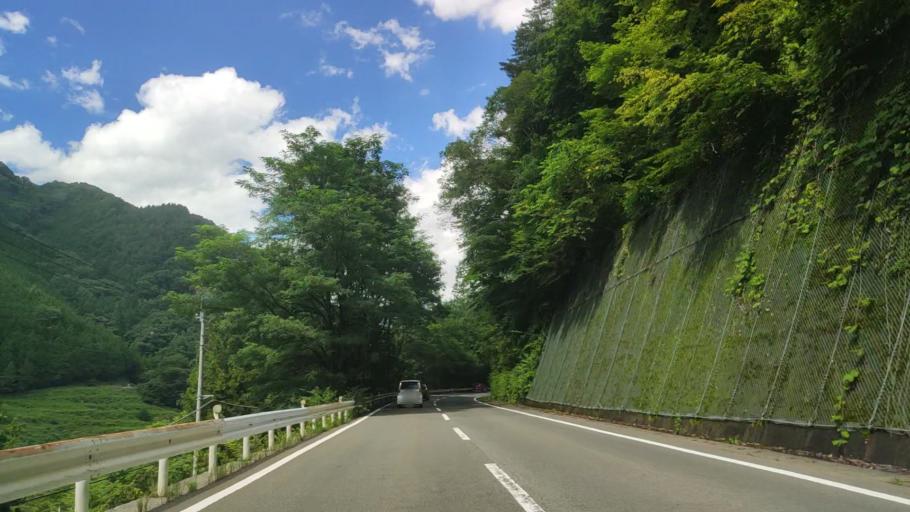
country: JP
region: Yamanashi
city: Enzan
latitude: 35.8208
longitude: 138.7589
